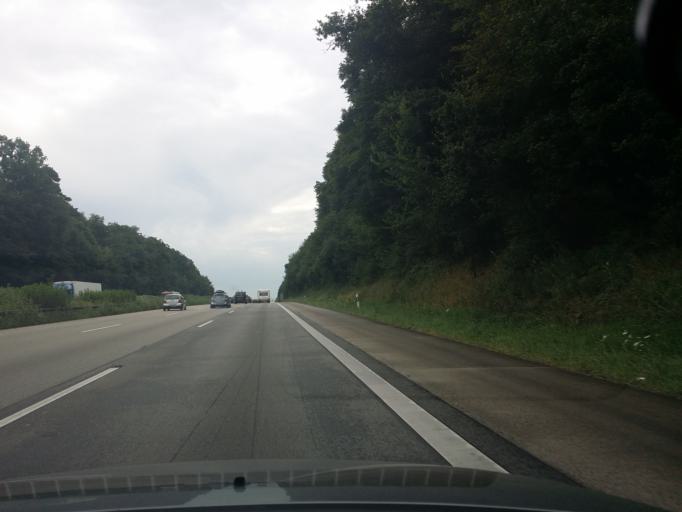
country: DE
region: Hesse
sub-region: Regierungsbezirk Darmstadt
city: Idstein
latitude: 50.1759
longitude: 8.2775
